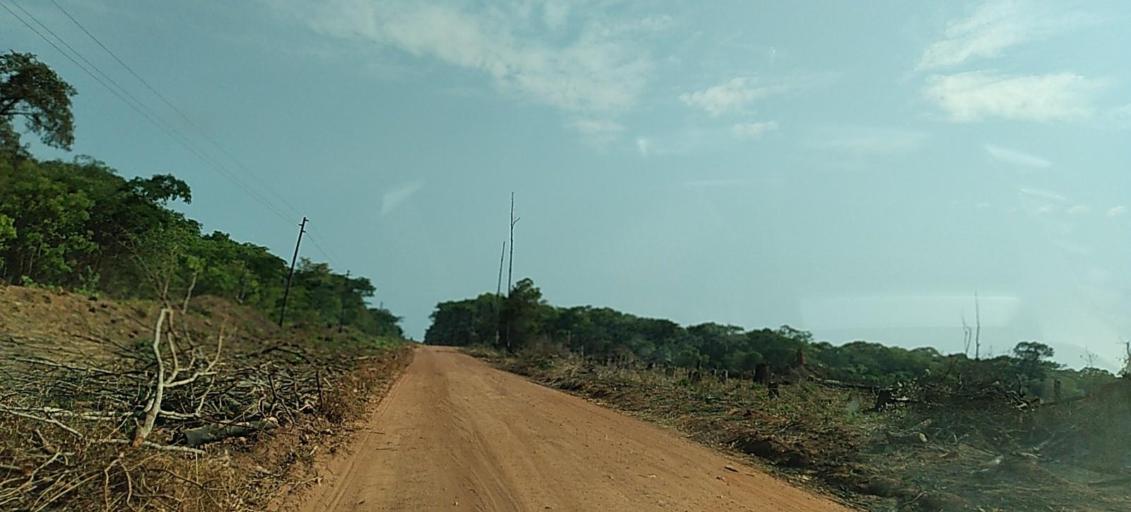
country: ZM
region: Copperbelt
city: Kalulushi
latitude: -12.9922
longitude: 27.8148
